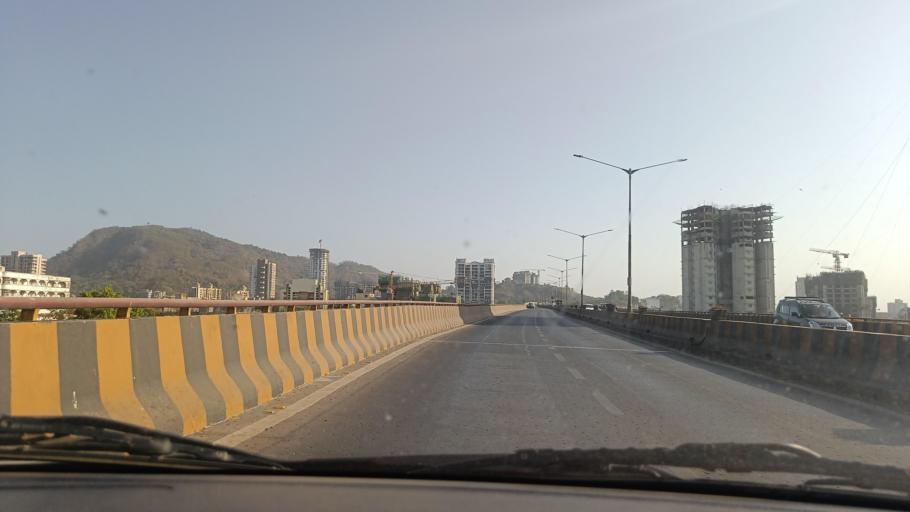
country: IN
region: Maharashtra
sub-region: Mumbai Suburban
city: Mumbai
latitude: 19.0502
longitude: 72.9105
